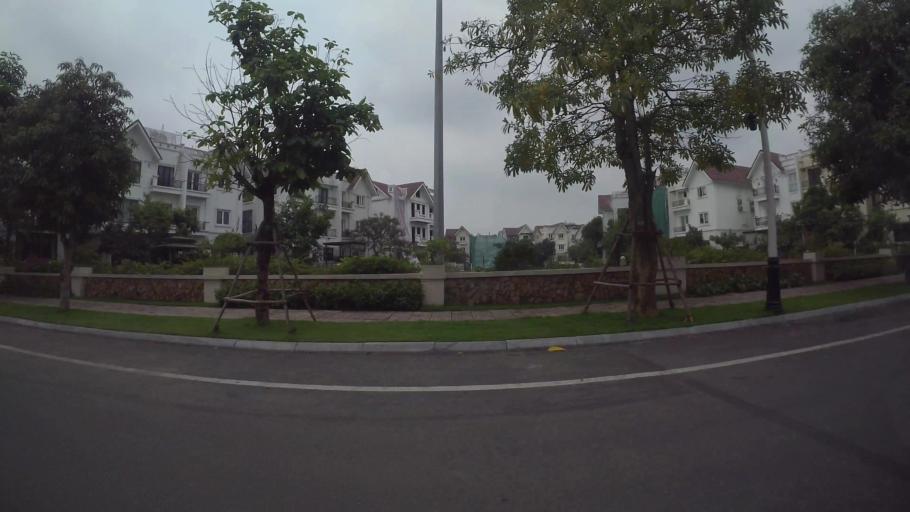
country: VN
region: Ha Noi
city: Trau Quy
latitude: 21.0415
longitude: 105.9212
